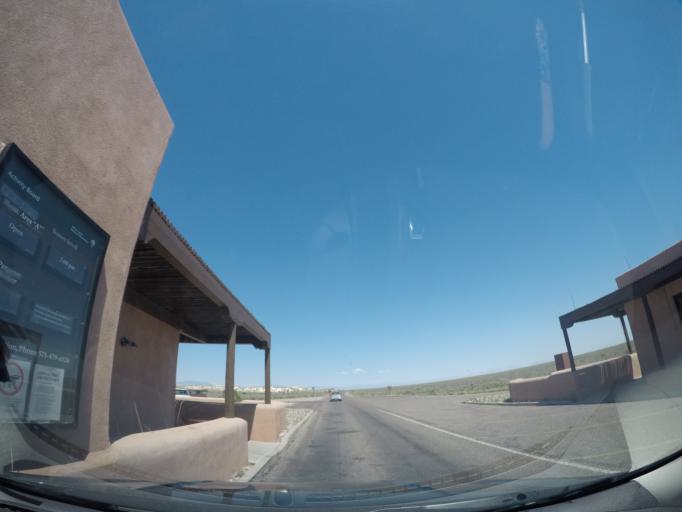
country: US
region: New Mexico
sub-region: Otero County
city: Holloman Air Force Base
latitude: 32.7825
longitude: -106.1757
